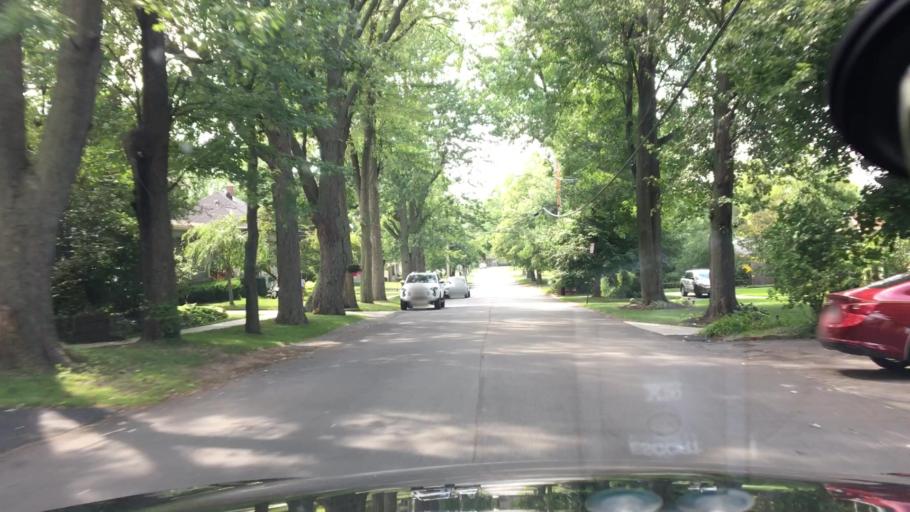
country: US
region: New York
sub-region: Erie County
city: Williamsville
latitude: 42.9680
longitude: -78.7397
